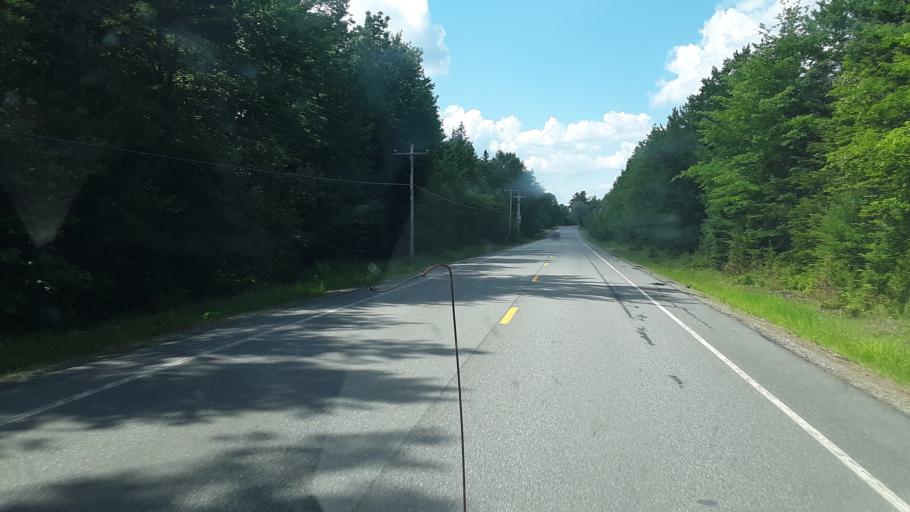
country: US
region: Maine
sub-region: Washington County
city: Machias
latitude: 45.0185
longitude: -67.5579
